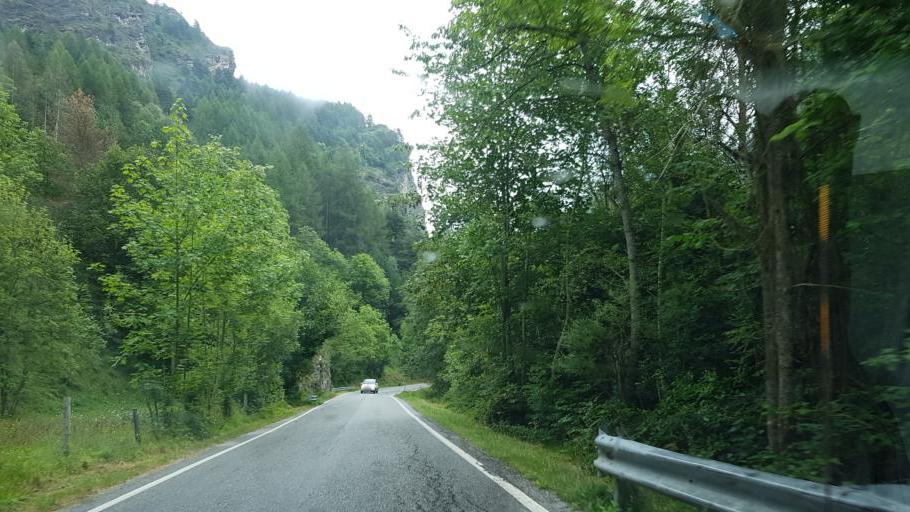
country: IT
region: Piedmont
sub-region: Provincia di Cuneo
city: Prazzo Superiore
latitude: 44.4871
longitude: 7.0769
